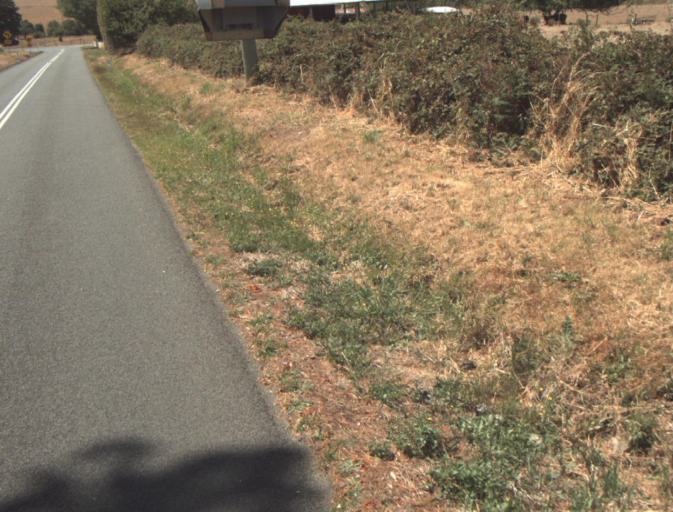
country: AU
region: Tasmania
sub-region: Launceston
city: Mayfield
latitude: -41.2662
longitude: 147.1326
